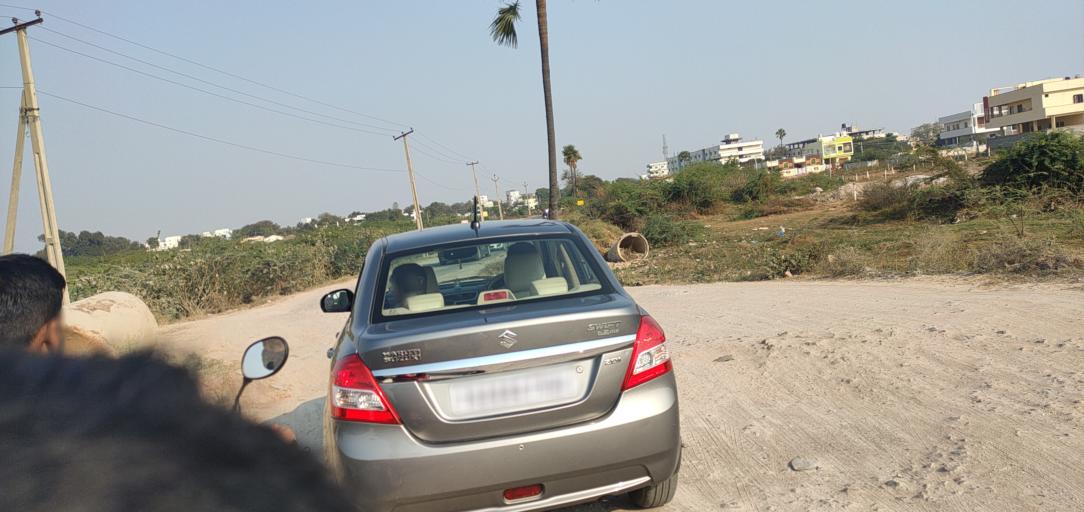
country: IN
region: Telangana
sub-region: Rangareddi
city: Lal Bahadur Nagar
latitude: 17.3424
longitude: 78.6200
